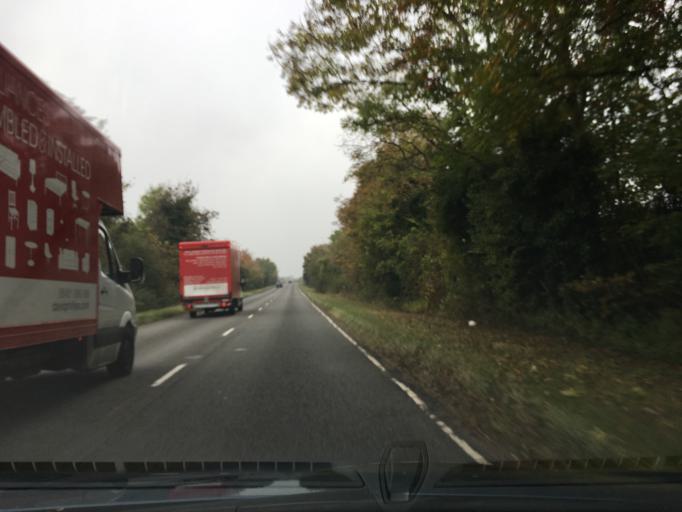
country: GB
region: England
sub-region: Surrey
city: Normandy
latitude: 51.2267
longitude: -0.6676
